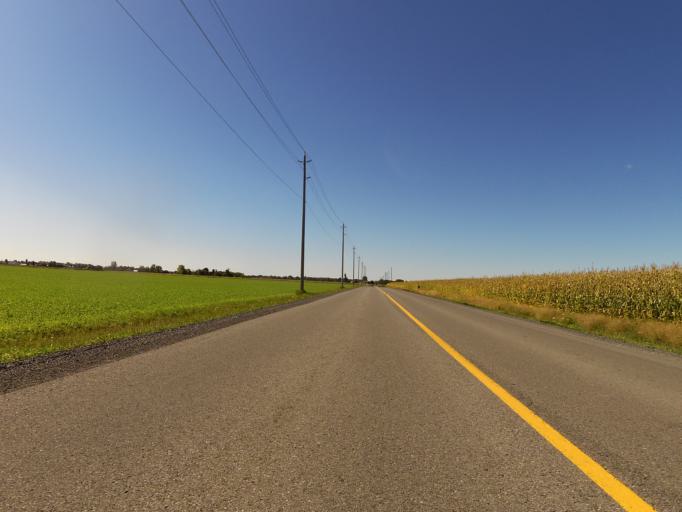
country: CA
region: Ontario
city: Casselman
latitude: 45.2664
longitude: -75.2555
